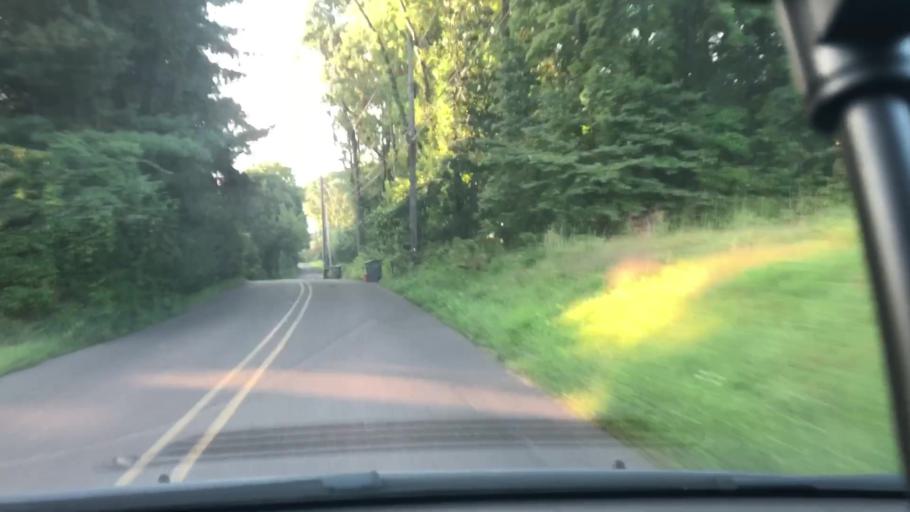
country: US
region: Pennsylvania
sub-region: Chester County
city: Kenilworth
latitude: 40.1839
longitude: -75.6418
